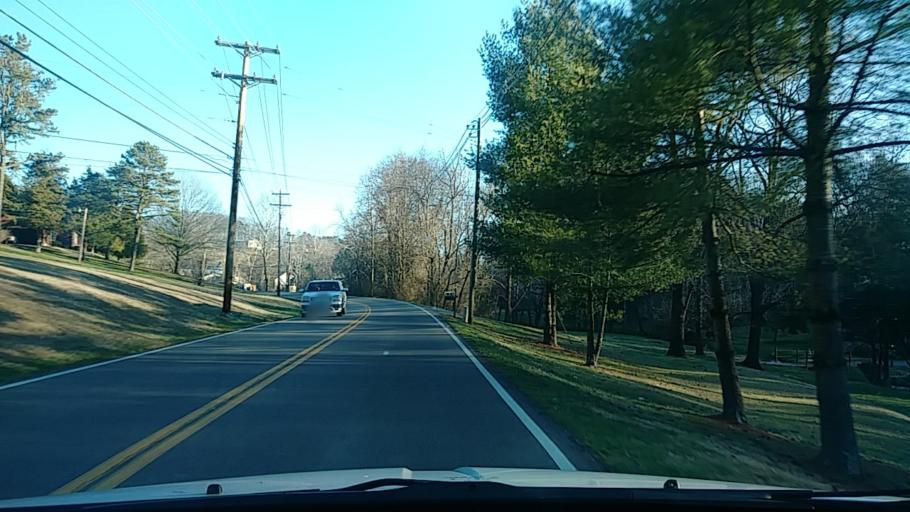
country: US
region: Tennessee
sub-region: Hamblen County
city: Morristown
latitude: 36.1899
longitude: -83.3858
